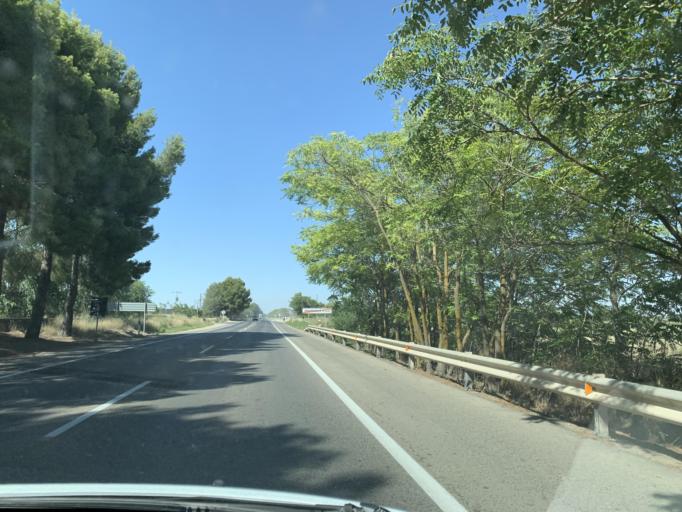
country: ES
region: Castille-La Mancha
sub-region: Provincia de Ciudad Real
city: Argamasilla de Alba
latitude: 39.1345
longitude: -3.0771
